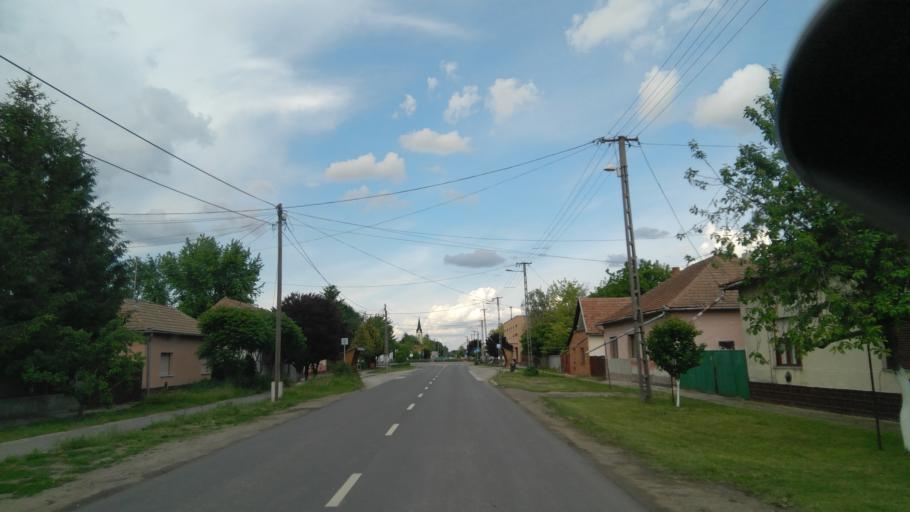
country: HU
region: Bekes
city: Dombegyhaz
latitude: 46.3380
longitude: 21.1303
